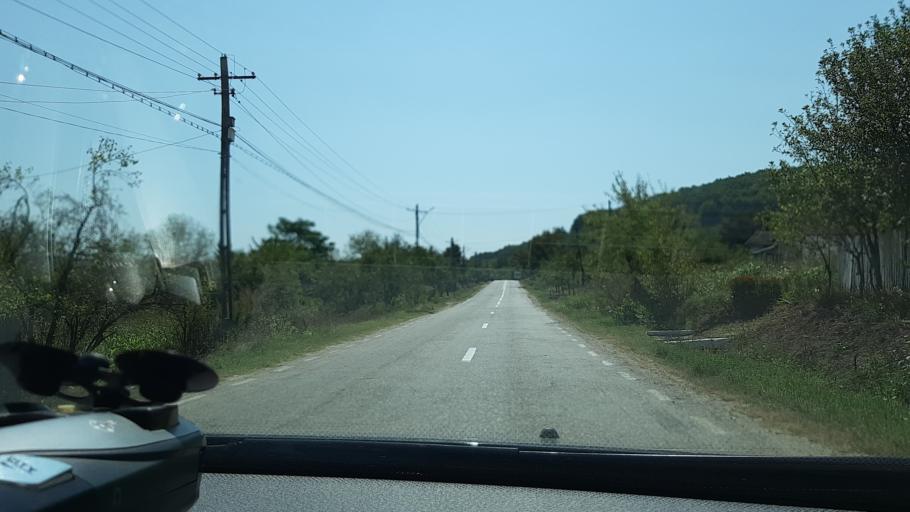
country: RO
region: Gorj
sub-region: Comuna Hurezani
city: Hurezani
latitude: 44.8294
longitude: 23.6430
